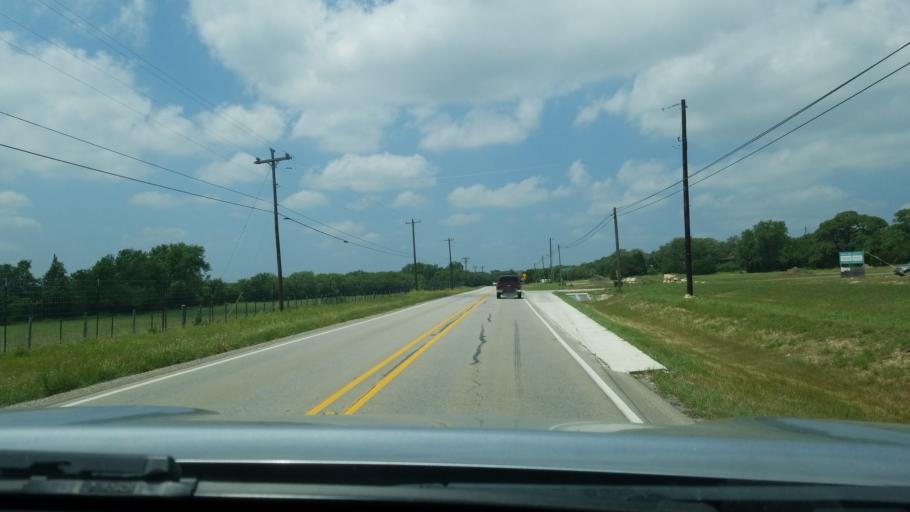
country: US
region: Texas
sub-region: Hays County
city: Dripping Springs
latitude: 30.1605
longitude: -98.0782
